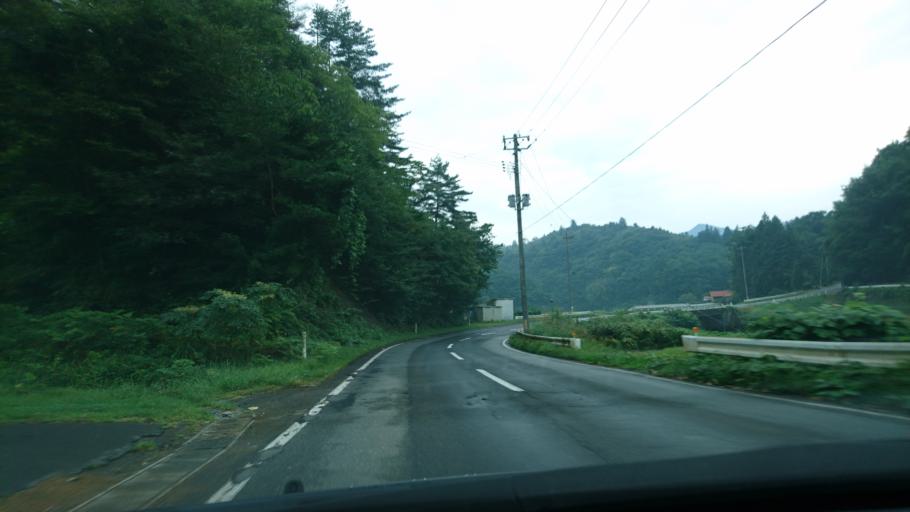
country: JP
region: Iwate
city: Ichinoseki
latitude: 39.0161
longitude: 141.2483
